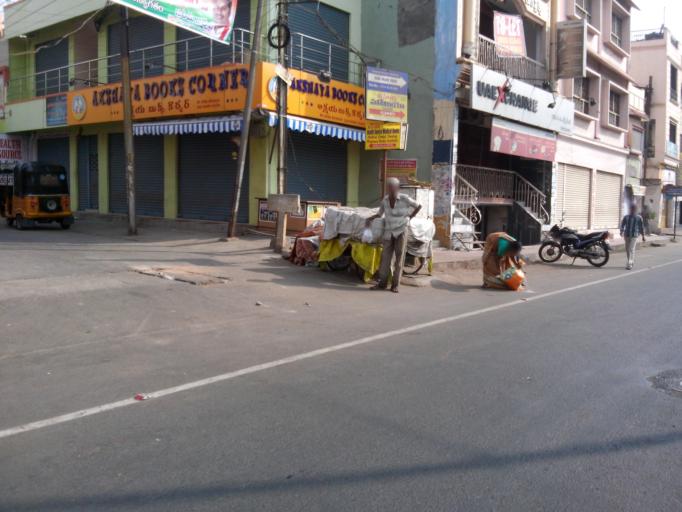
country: IN
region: Andhra Pradesh
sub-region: Krishna
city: Vijayawada
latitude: 16.5138
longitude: 80.6282
